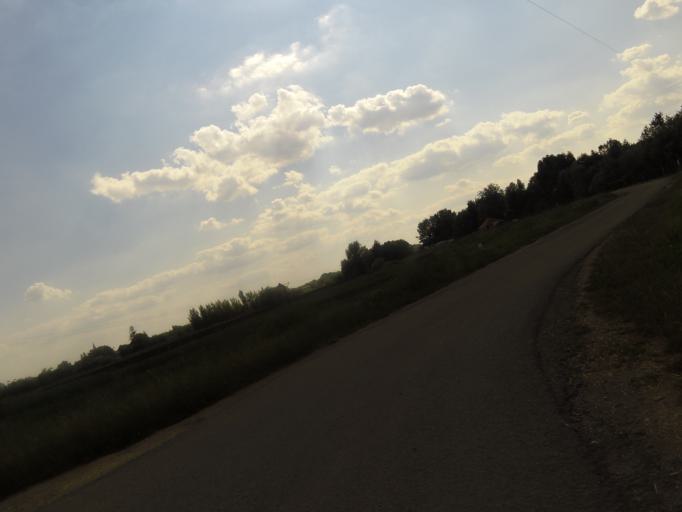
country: HU
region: Jasz-Nagykun-Szolnok
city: Tiszafured
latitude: 47.6087
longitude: 20.7225
